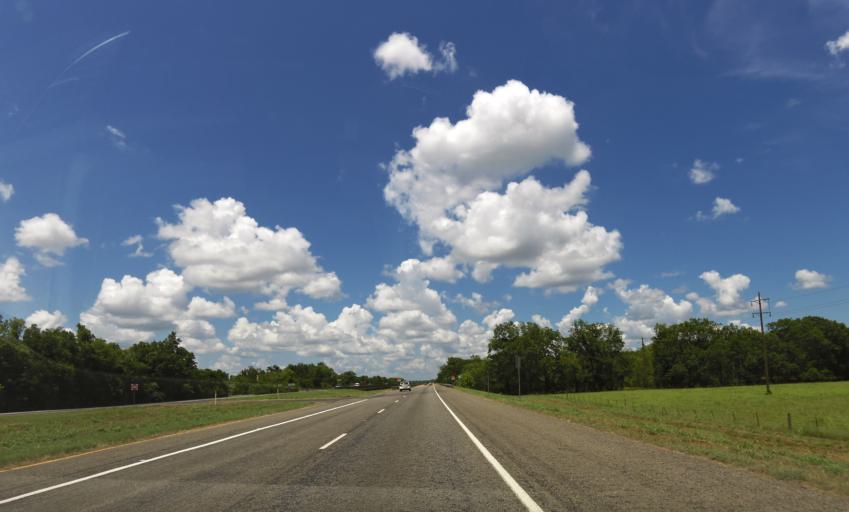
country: US
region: Texas
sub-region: San Jacinto County
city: Shepherd
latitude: 30.5660
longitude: -94.9529
